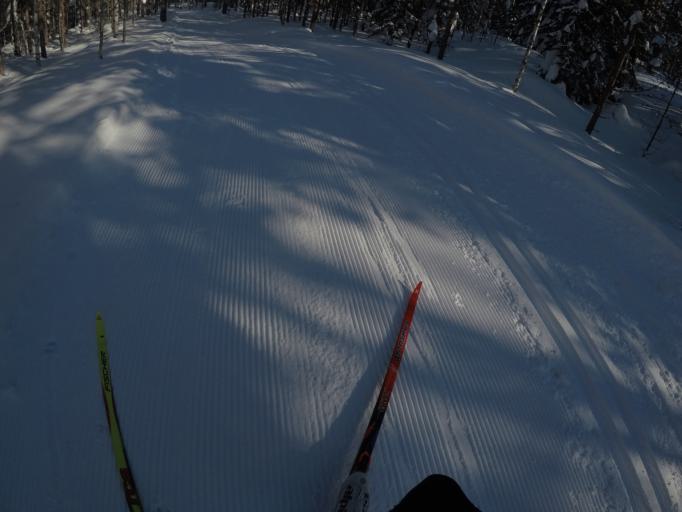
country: SE
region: Vaesternorrland
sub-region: Sundsvalls Kommun
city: Sundsvall
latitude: 62.3652
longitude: 17.2963
